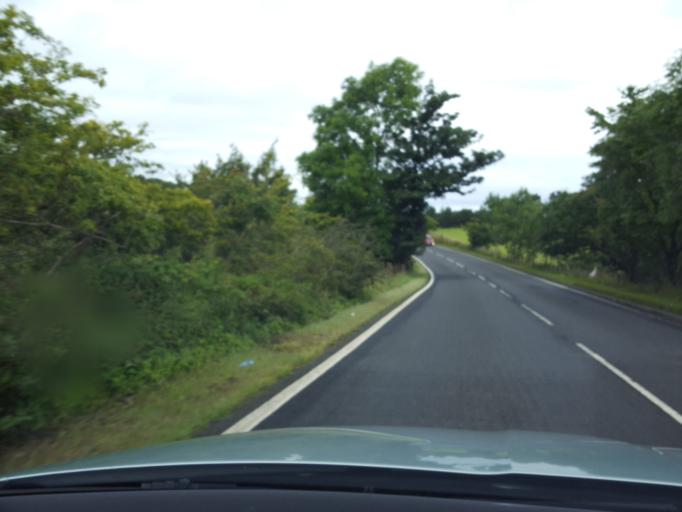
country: GB
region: Scotland
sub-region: Falkirk
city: Polmont
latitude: 55.9538
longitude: -3.6863
